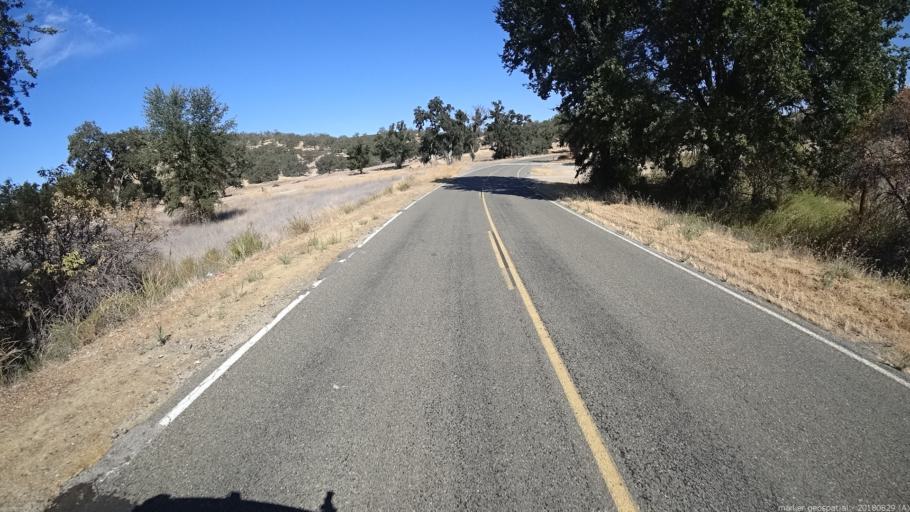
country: US
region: California
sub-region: San Luis Obispo County
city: Lake Nacimiento
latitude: 35.8980
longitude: -121.0903
